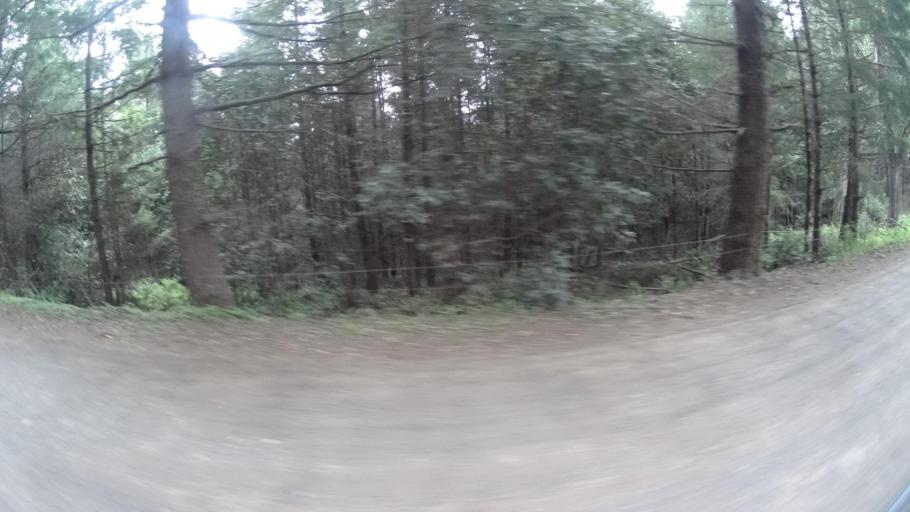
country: US
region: California
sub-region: Humboldt County
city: Redway
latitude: 40.2434
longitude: -123.7661
